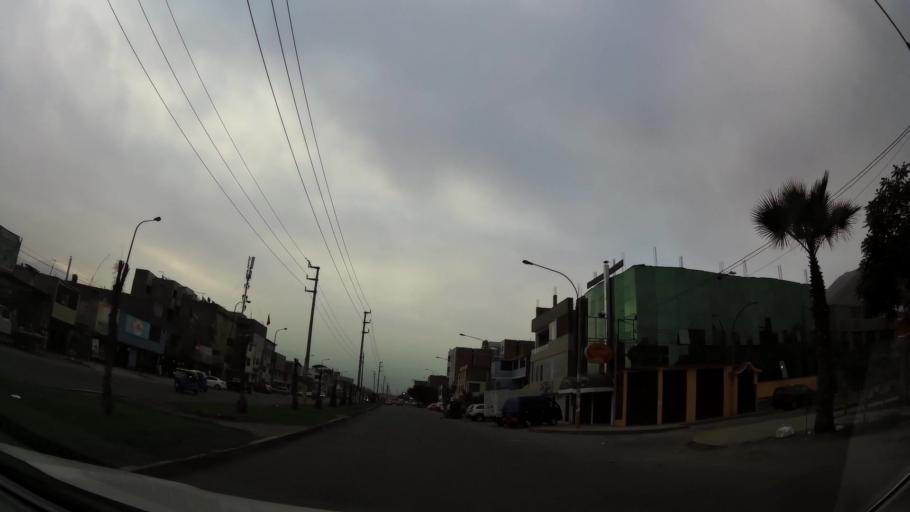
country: PE
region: Lima
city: Lima
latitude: -12.0046
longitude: -76.9982
